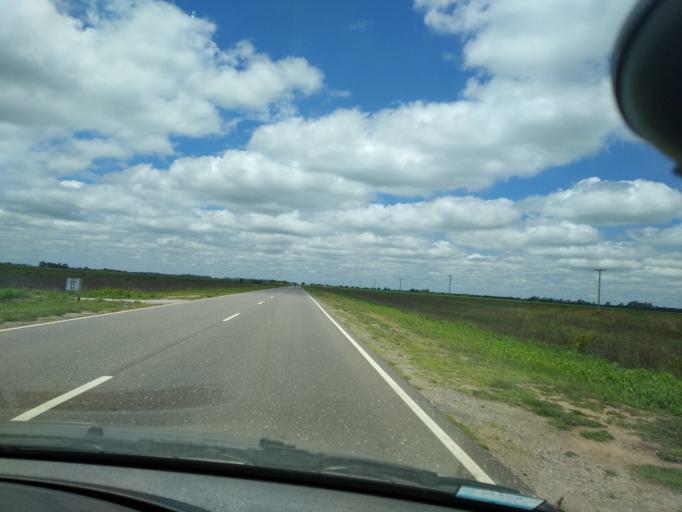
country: AR
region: Cordoba
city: Toledo
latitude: -31.6452
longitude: -64.0147
